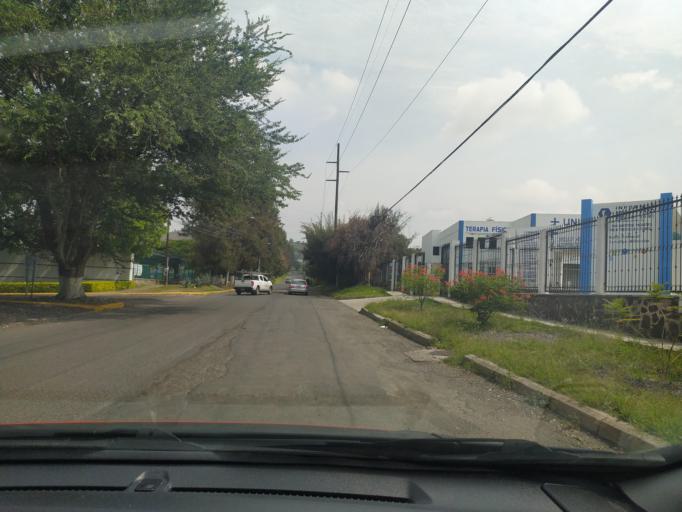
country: MX
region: Jalisco
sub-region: Tlajomulco de Zuniga
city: La Tijera
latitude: 20.6036
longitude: -103.4060
